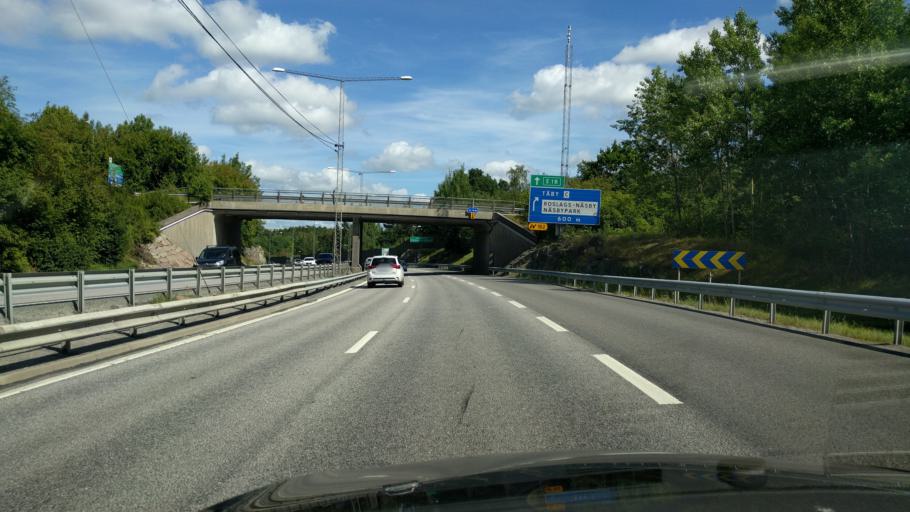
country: SE
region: Stockholm
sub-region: Taby Kommun
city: Taby
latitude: 59.4266
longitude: 18.0631
